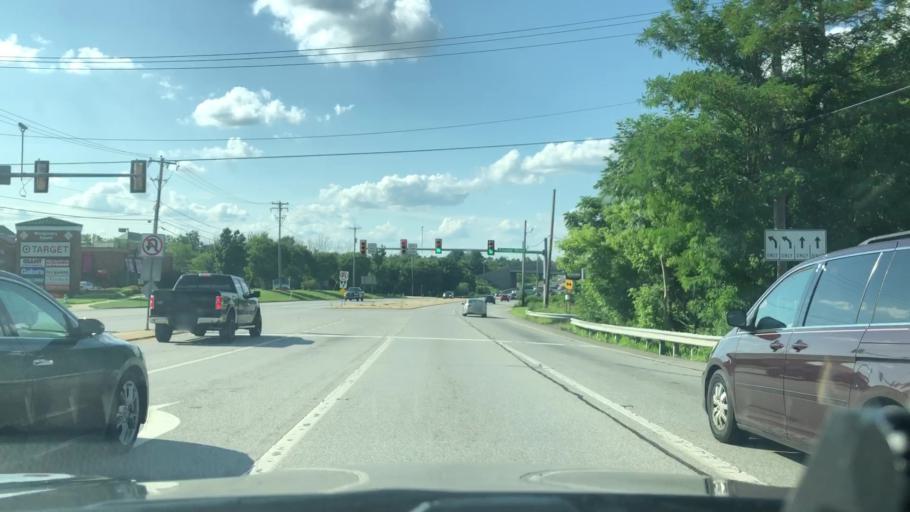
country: US
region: Pennsylvania
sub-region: Montgomery County
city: Montgomeryville
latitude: 40.2286
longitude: -75.2364
